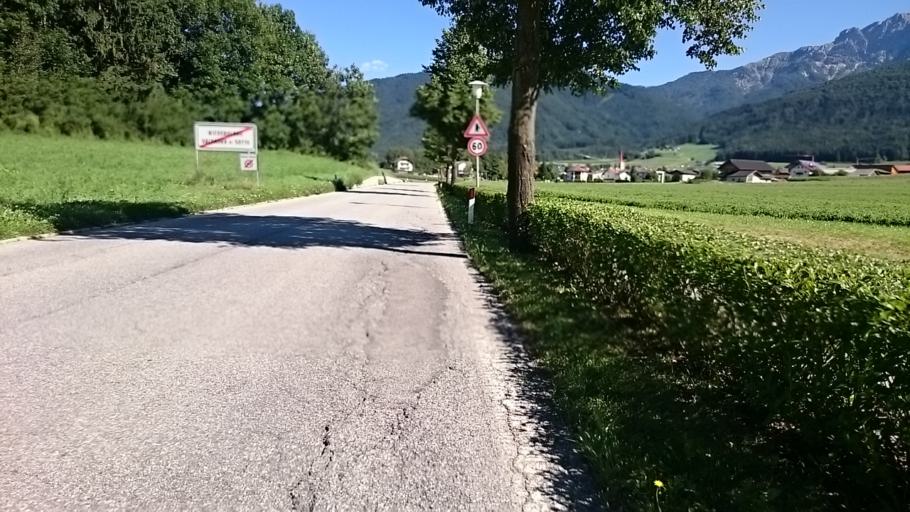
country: IT
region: Trentino-Alto Adige
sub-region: Bolzano
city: Valdaora di Mezzo
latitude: 46.7664
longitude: 12.0233
